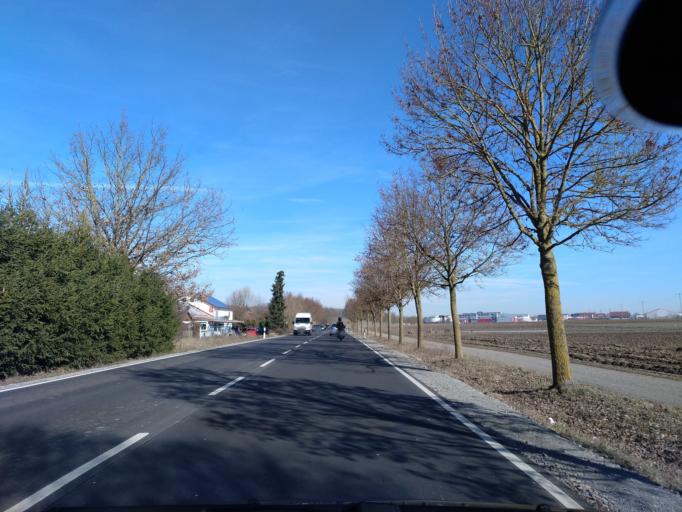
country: DE
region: Baden-Wuerttemberg
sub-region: Regierungsbezirk Stuttgart
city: Michelfeld
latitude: 49.0993
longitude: 9.6825
